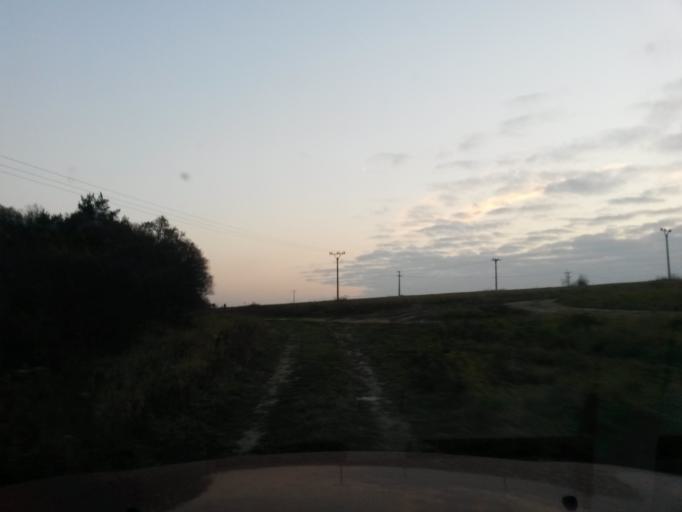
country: SK
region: Kosicky
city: Kosice
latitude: 48.7142
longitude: 21.2935
